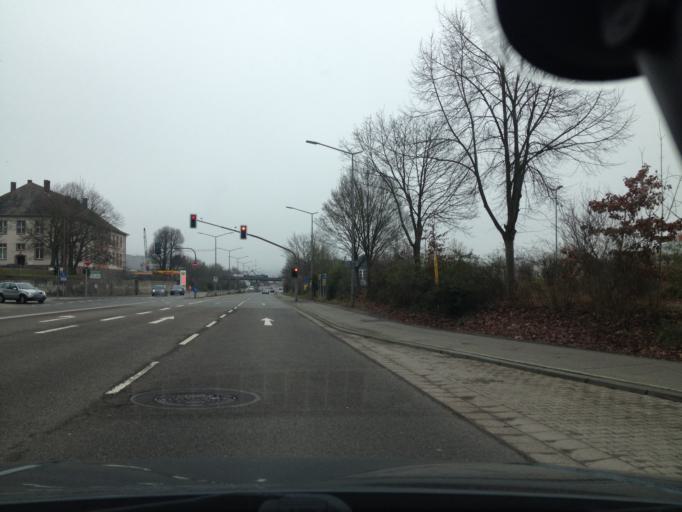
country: DE
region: Saarland
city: Homburg
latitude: 49.3292
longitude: 7.3221
